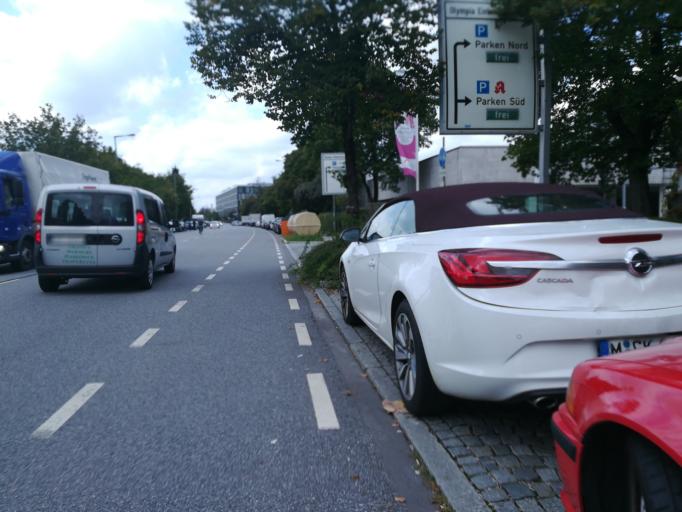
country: DE
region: Bavaria
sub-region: Upper Bavaria
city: Munich
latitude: 48.1820
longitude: 11.5357
